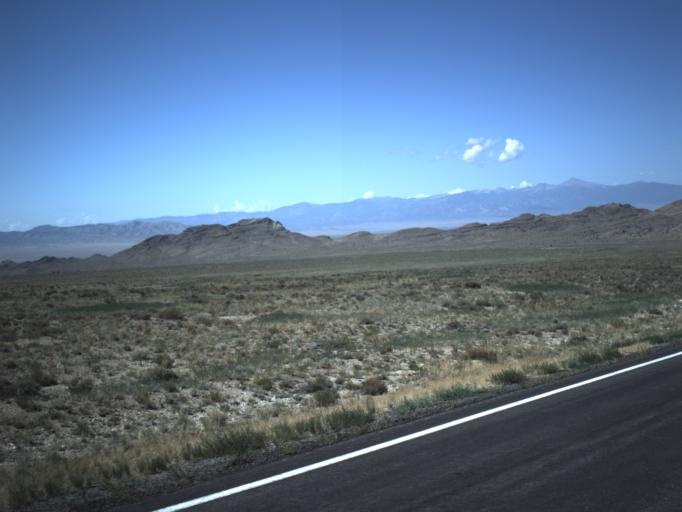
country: US
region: Utah
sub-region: Beaver County
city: Milford
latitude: 39.0731
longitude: -113.6661
